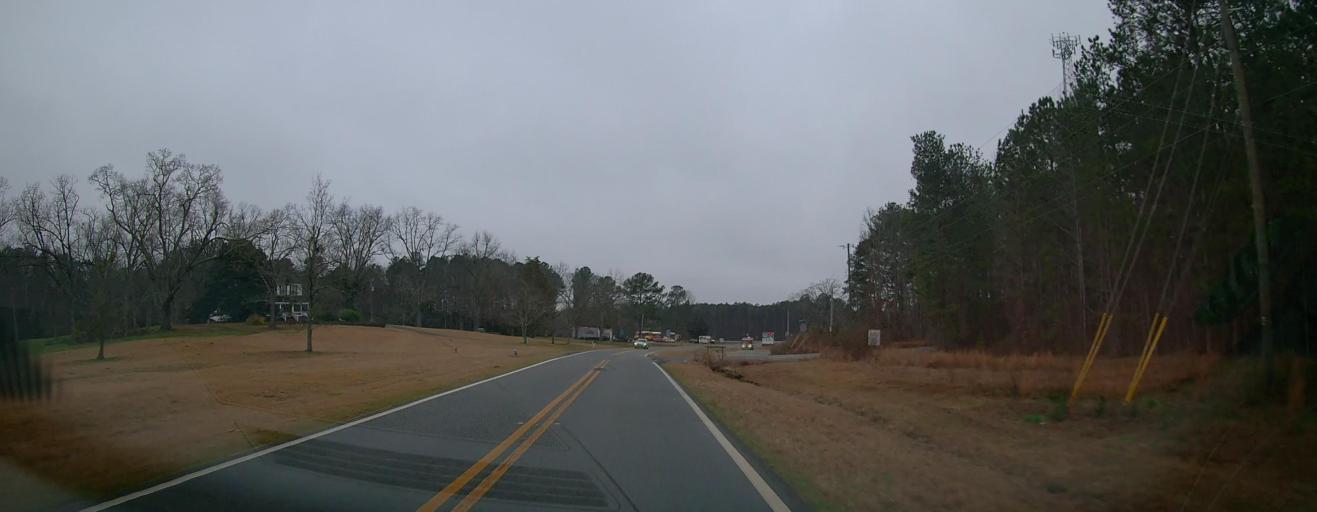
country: US
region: Georgia
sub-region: Monroe County
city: Forsyth
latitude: 33.1132
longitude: -83.9990
